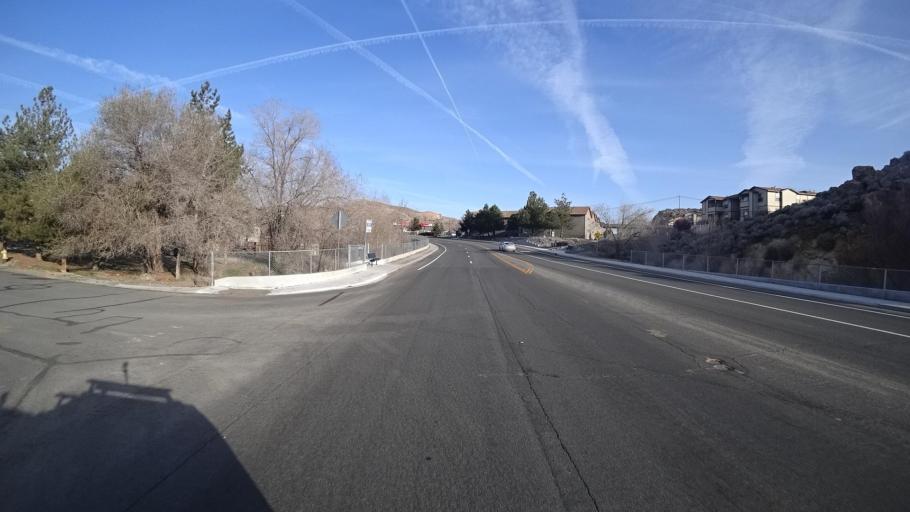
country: US
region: Nevada
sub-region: Washoe County
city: Sun Valley
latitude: 39.5696
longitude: -119.7802
